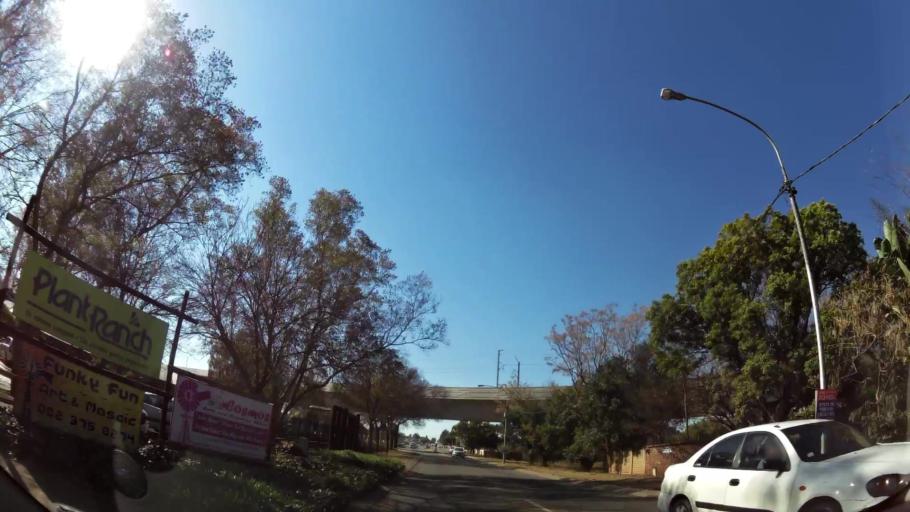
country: ZA
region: Gauteng
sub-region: City of Tshwane Metropolitan Municipality
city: Centurion
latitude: -25.8436
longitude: 28.1843
